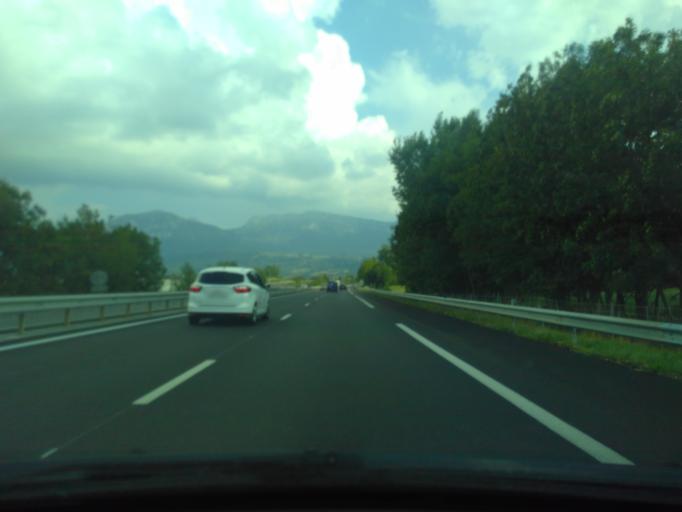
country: FR
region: Rhone-Alpes
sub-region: Departement de la Haute-Savoie
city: Cornier
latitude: 46.0805
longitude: 6.2891
